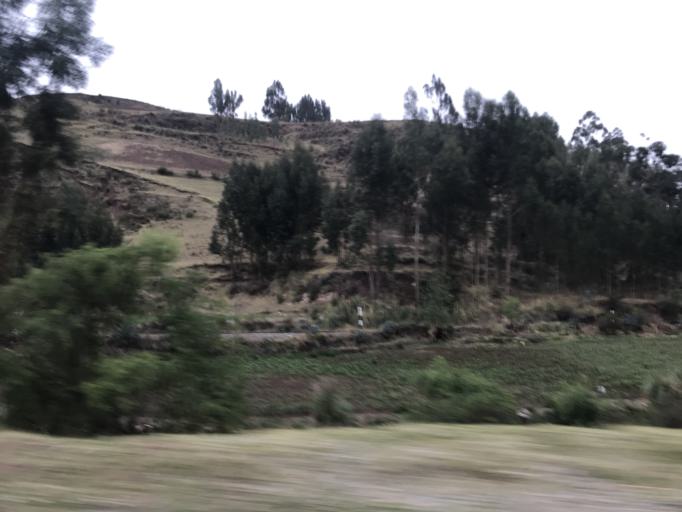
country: PE
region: Cusco
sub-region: Provincia de Anta
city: Huarocondo
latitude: -13.3983
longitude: -72.2110
